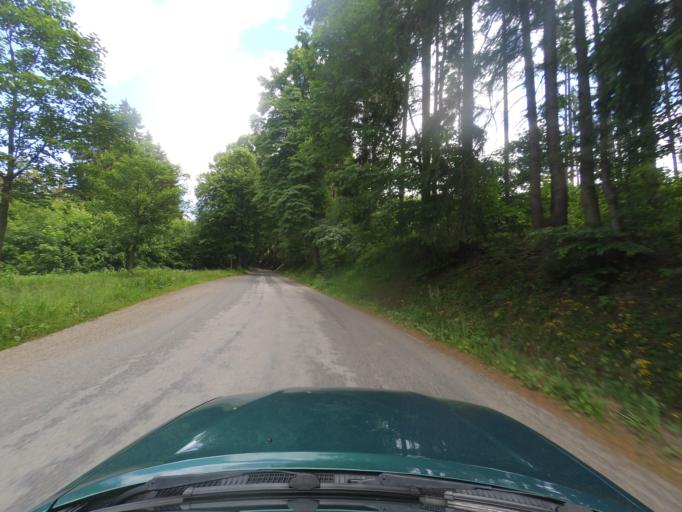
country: CZ
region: Pardubicky
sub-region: Okres Usti nad Orlici
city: Kunvald
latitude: 50.1160
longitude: 16.5700
